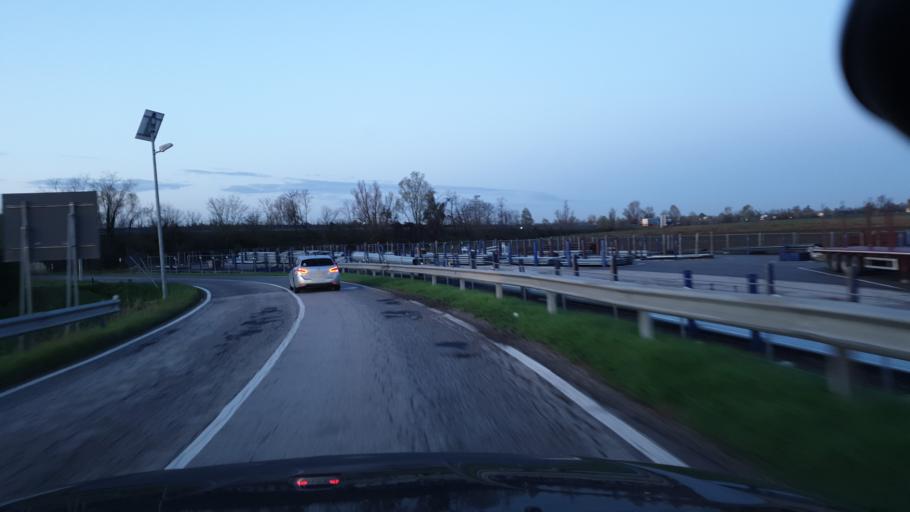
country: IT
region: Veneto
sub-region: Provincia di Rovigo
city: Fratta Polesine
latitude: 45.0229
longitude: 11.6382
